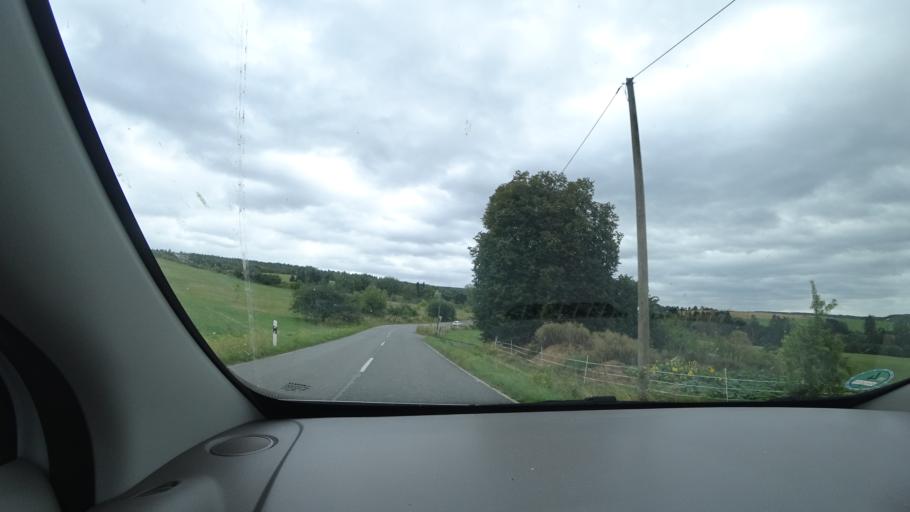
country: DE
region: Rheinland-Pfalz
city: Hohr-Grenzhausen
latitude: 50.4255
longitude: 7.6792
